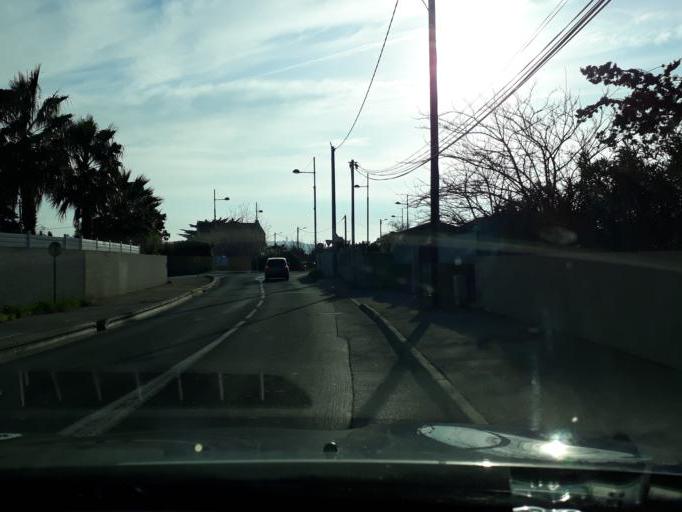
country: FR
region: Languedoc-Roussillon
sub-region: Departement de l'Herault
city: Marseillan
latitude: 43.3211
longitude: 3.5367
